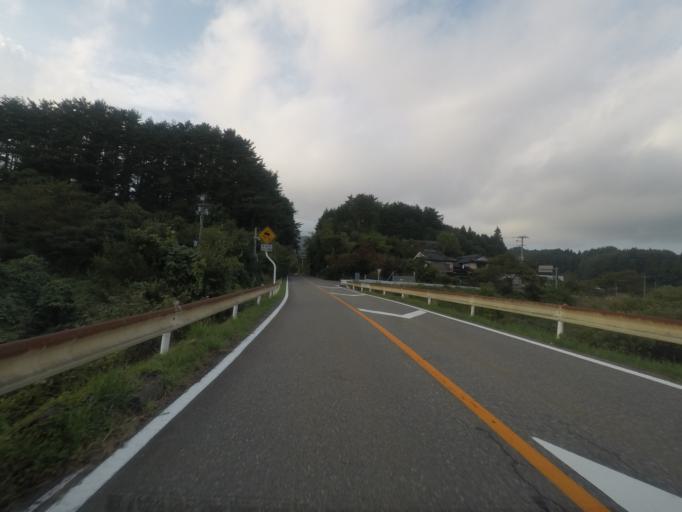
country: JP
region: Fukushima
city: Funehikimachi-funehiki
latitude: 37.5650
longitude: 140.7439
